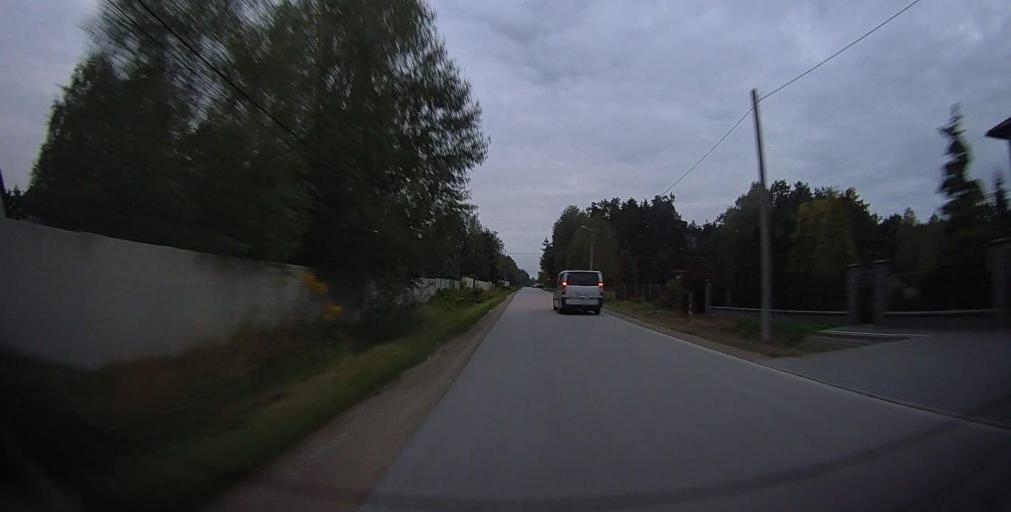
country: PL
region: Masovian Voivodeship
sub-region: Powiat radomski
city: Jedlinsk
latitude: 51.4667
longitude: 21.1293
